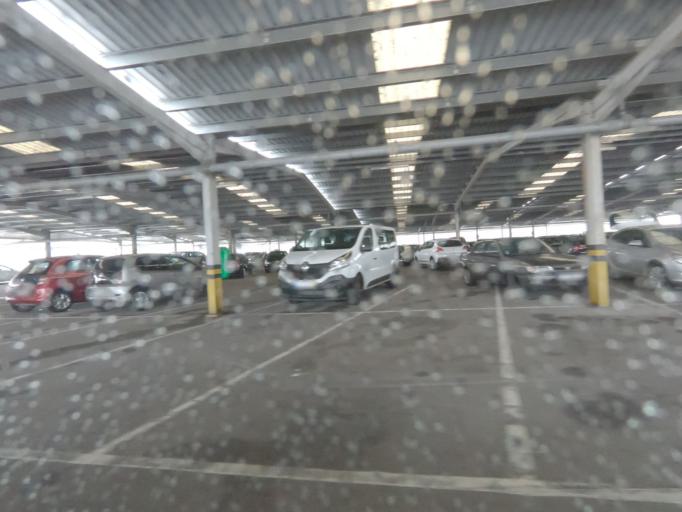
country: PT
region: Porto
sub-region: Penafiel
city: Penafiel
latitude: 41.1936
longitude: -8.3062
